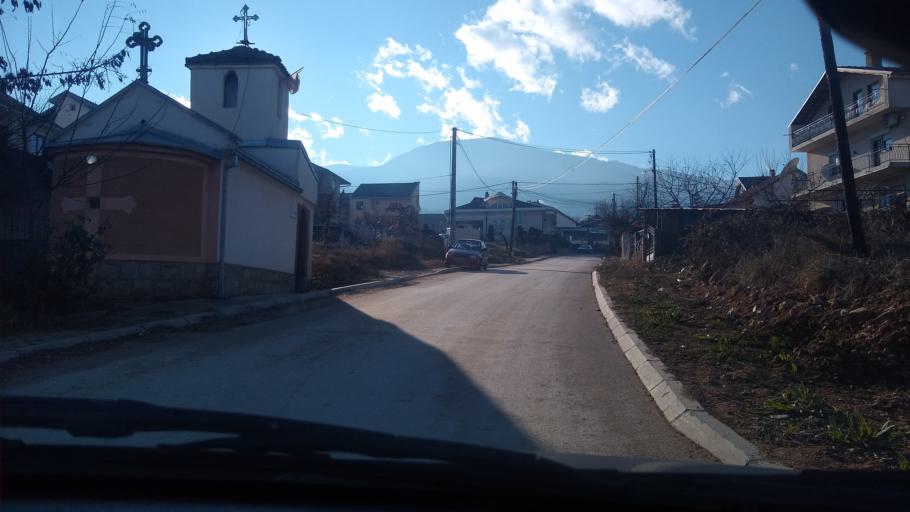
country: MK
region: Bitola
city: Bitola
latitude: 41.0194
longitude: 21.3154
